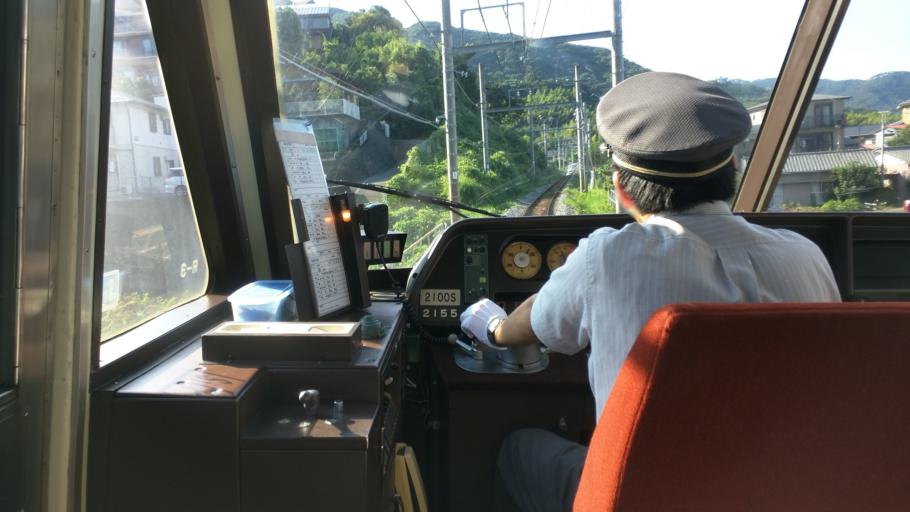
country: JP
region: Shizuoka
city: Atami
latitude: 35.0473
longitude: 139.0681
